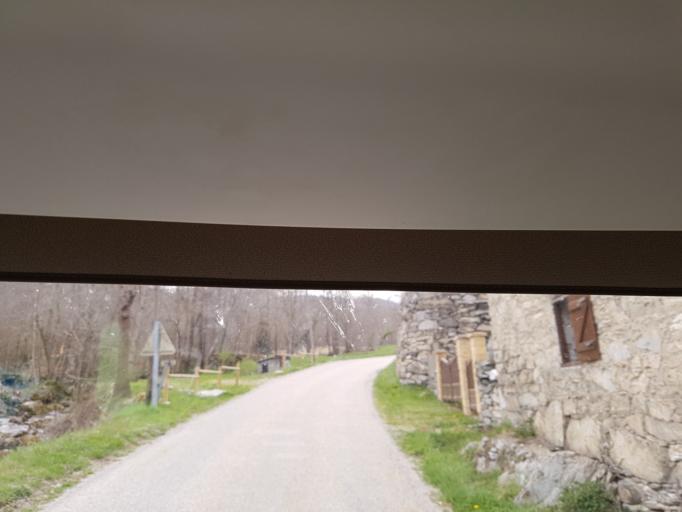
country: FR
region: Languedoc-Roussillon
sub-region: Departement de l'Aude
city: Quillan
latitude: 42.7342
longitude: 2.0851
